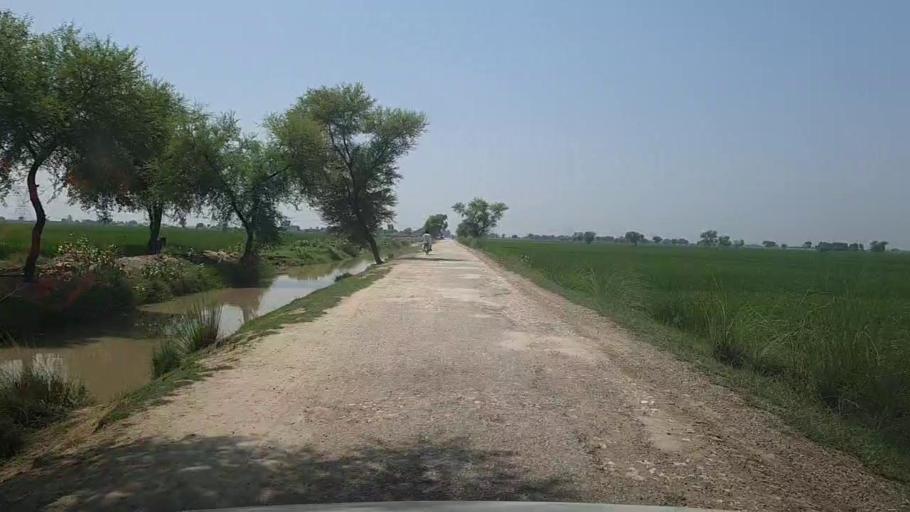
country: PK
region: Sindh
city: Kashmor
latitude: 28.3314
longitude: 69.3880
